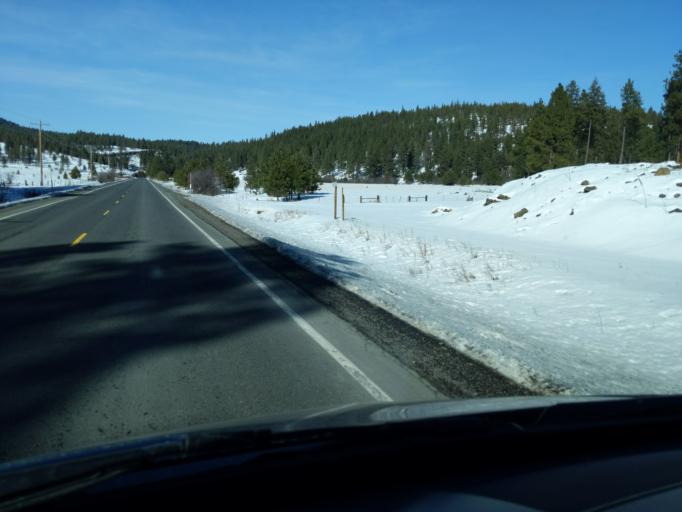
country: US
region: Oregon
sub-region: Grant County
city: John Day
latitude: 44.9255
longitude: -119.0101
